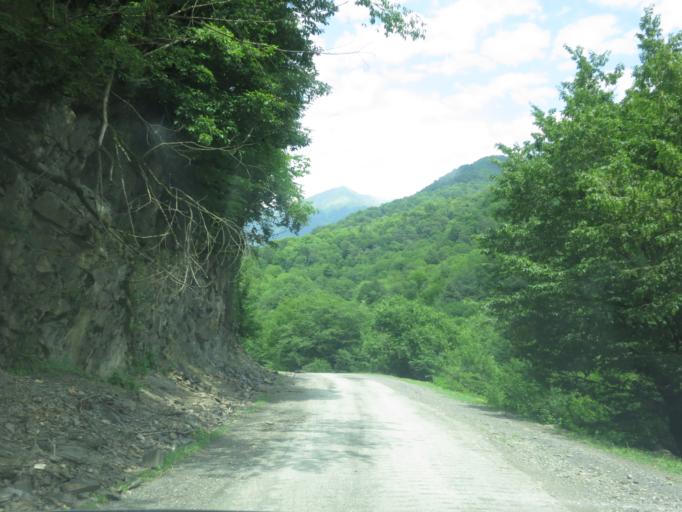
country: GE
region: Kakheti
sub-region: Telavi
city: Telavi
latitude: 42.1720
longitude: 45.4300
